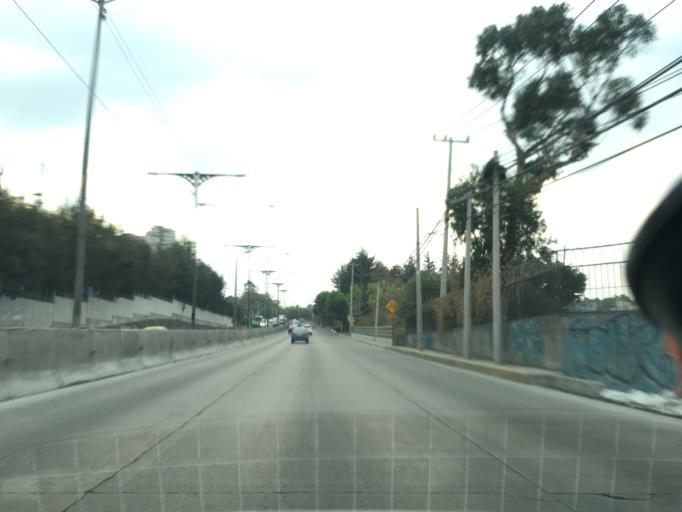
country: MX
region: Mexico City
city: Col. Bosques de las Lomas
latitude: 19.3749
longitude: -99.2641
